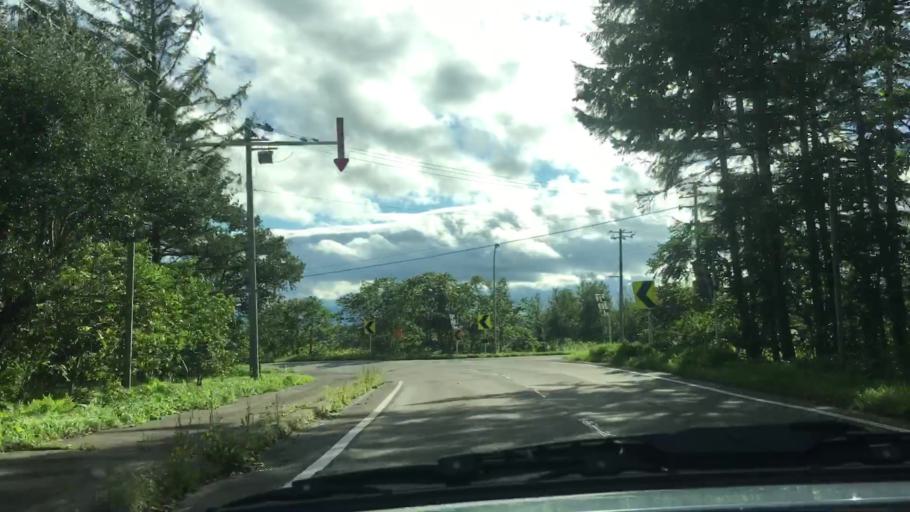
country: JP
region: Hokkaido
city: Otofuke
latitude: 43.1793
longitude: 143.0086
